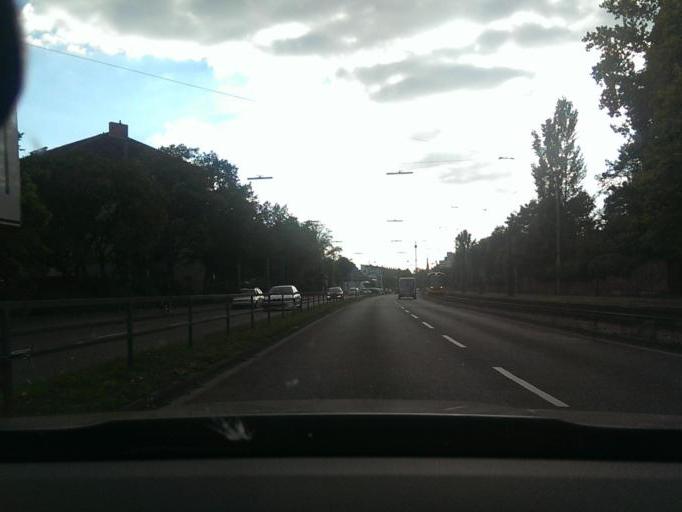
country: DE
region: Baden-Wuerttemberg
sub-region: Karlsruhe Region
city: Karlsruhe
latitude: 49.0166
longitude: 8.4380
